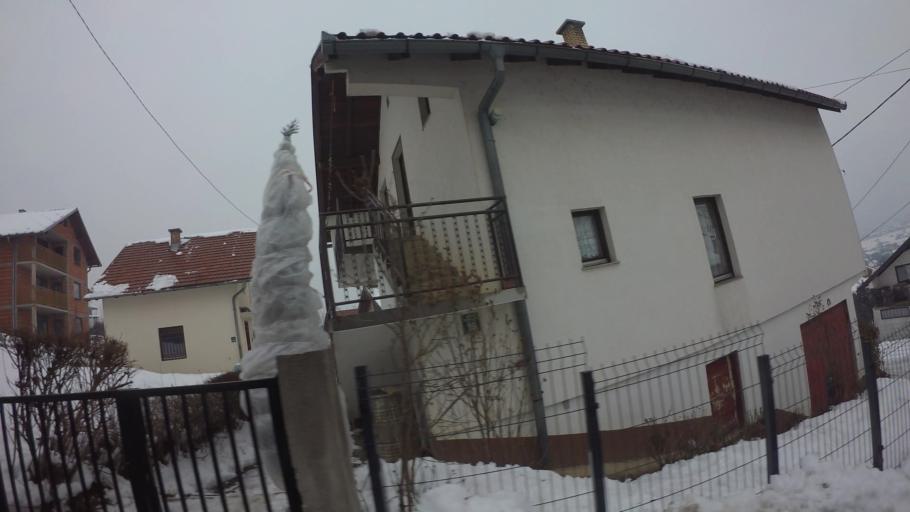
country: BA
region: Federation of Bosnia and Herzegovina
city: Hadzici
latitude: 43.8464
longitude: 18.2722
